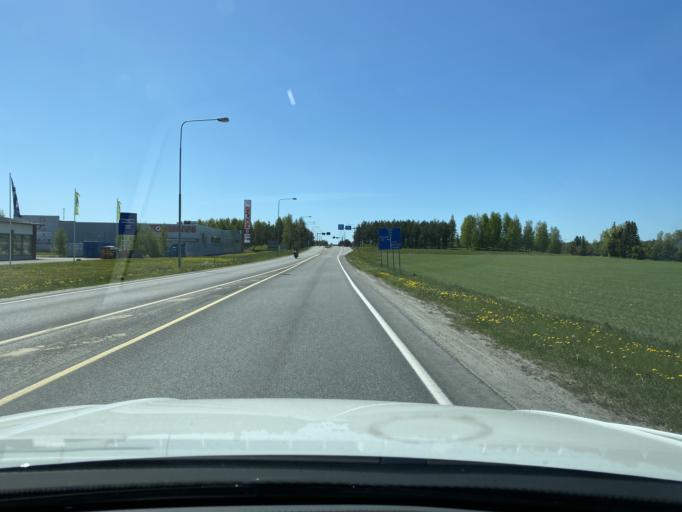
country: FI
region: Satakunta
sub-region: Pori
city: Huittinen
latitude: 61.1728
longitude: 22.6781
